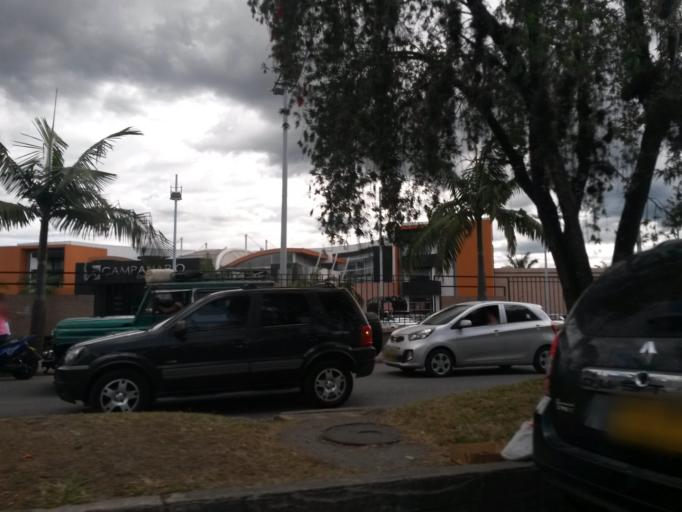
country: CO
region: Cauca
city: Popayan
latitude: 2.4598
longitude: -76.5935
